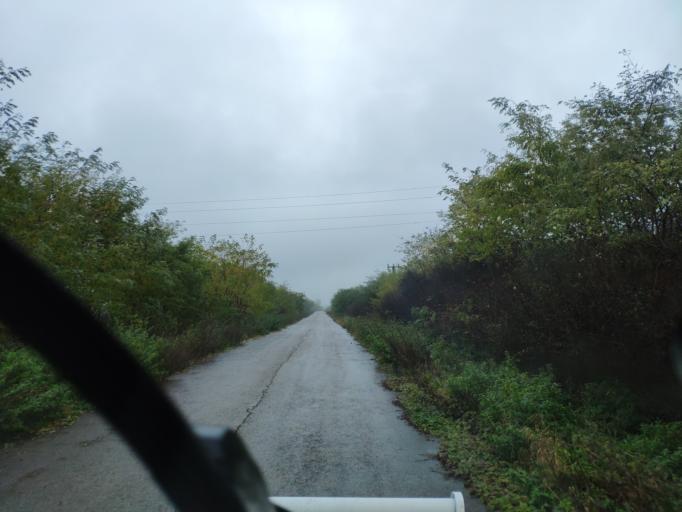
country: SK
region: Kosicky
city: Cierna nad Tisou
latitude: 48.4316
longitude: 22.0023
